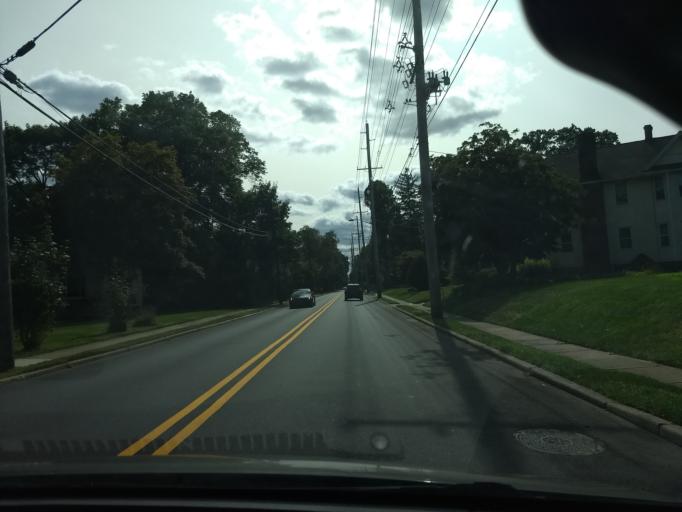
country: US
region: New Jersey
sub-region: Bergen County
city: Ridgewood
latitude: 40.9685
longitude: -74.1205
